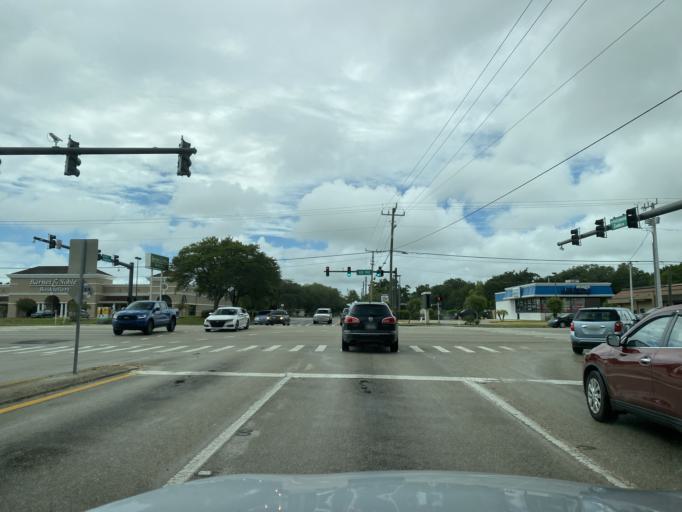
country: US
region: Florida
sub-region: Brevard County
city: West Melbourne
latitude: 28.0792
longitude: -80.6536
